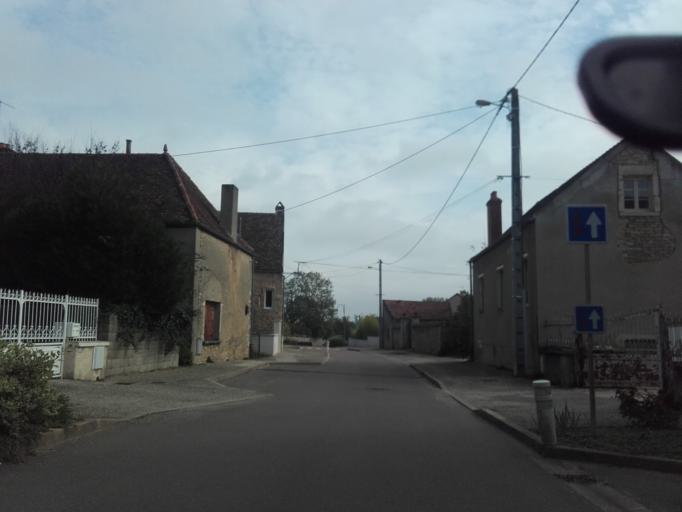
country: FR
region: Bourgogne
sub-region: Departement de la Cote-d'Or
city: Bligny-les-Beaune
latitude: 46.9853
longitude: 4.8270
